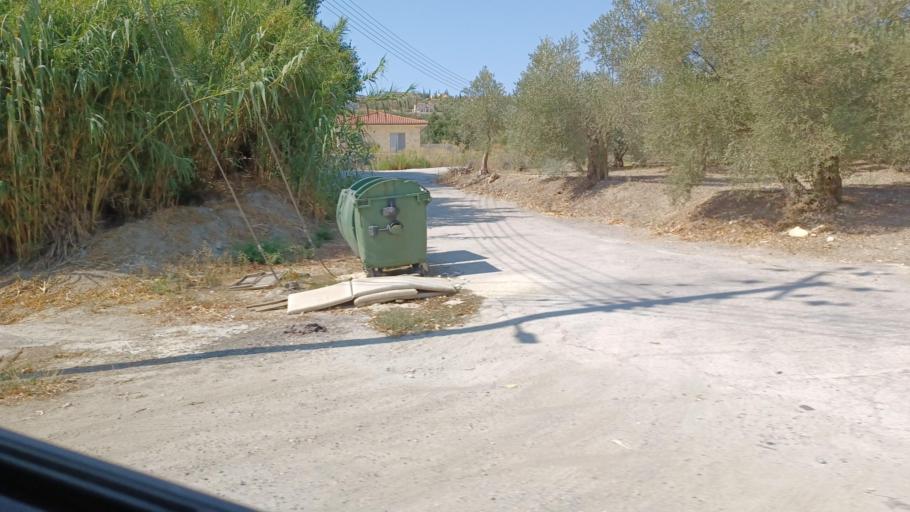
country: CY
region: Pafos
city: Tala
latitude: 34.9170
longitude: 32.4777
